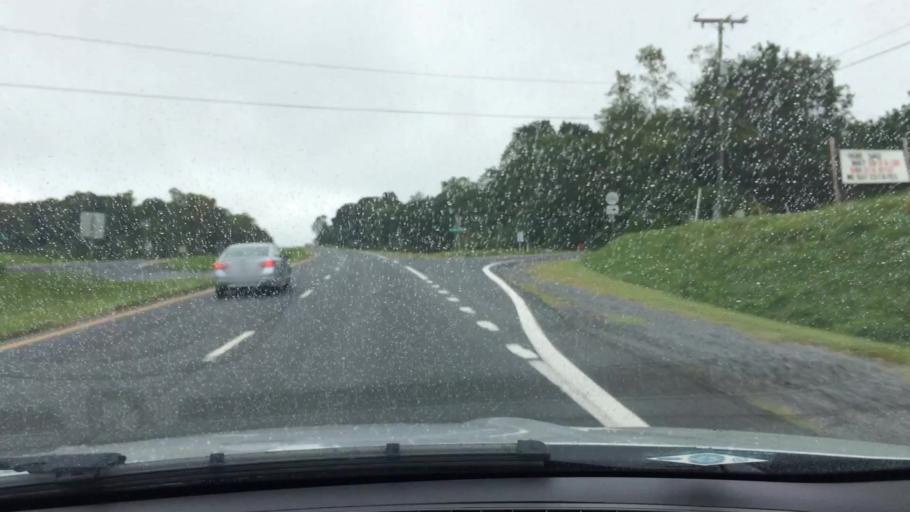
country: US
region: Virginia
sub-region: Campbell County
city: Rustburg
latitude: 37.2148
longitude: -79.1964
